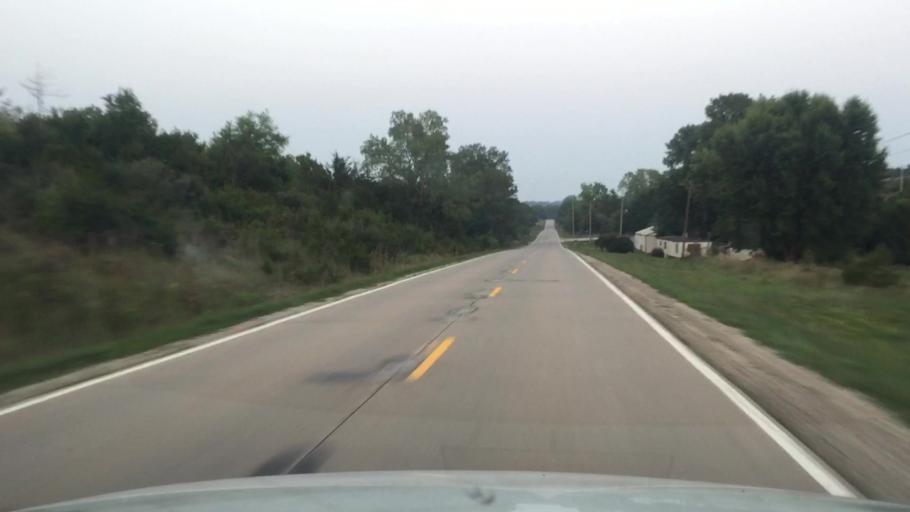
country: US
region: Iowa
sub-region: Warren County
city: Indianola
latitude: 41.1909
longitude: -93.6485
